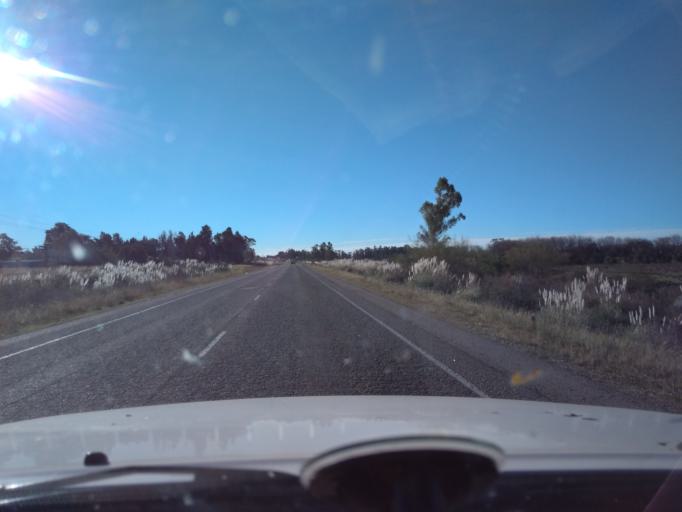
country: UY
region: Canelones
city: Sauce
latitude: -34.5997
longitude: -56.0503
